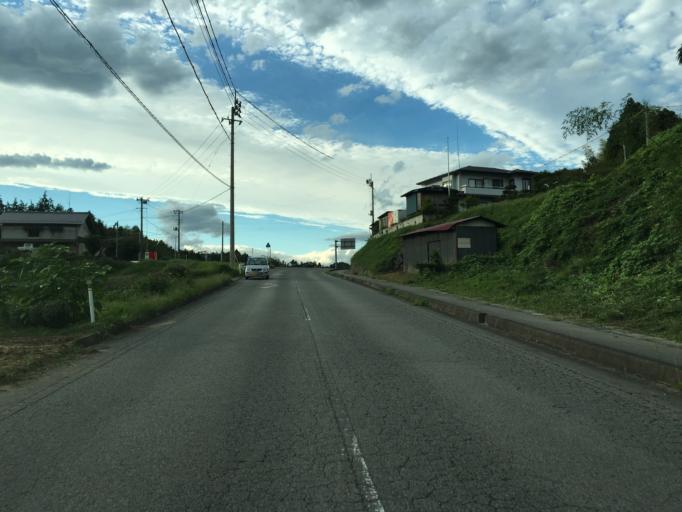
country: JP
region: Fukushima
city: Nihommatsu
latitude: 37.6085
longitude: 140.4972
